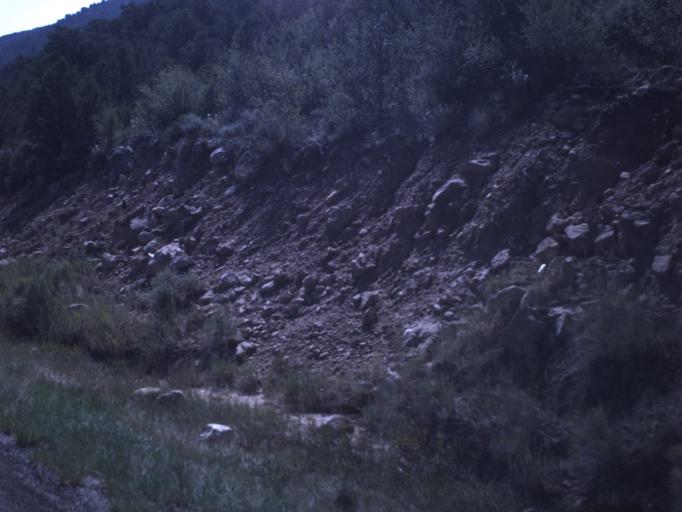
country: US
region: Utah
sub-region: Duchesne County
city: Duchesne
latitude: 40.2959
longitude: -110.5567
